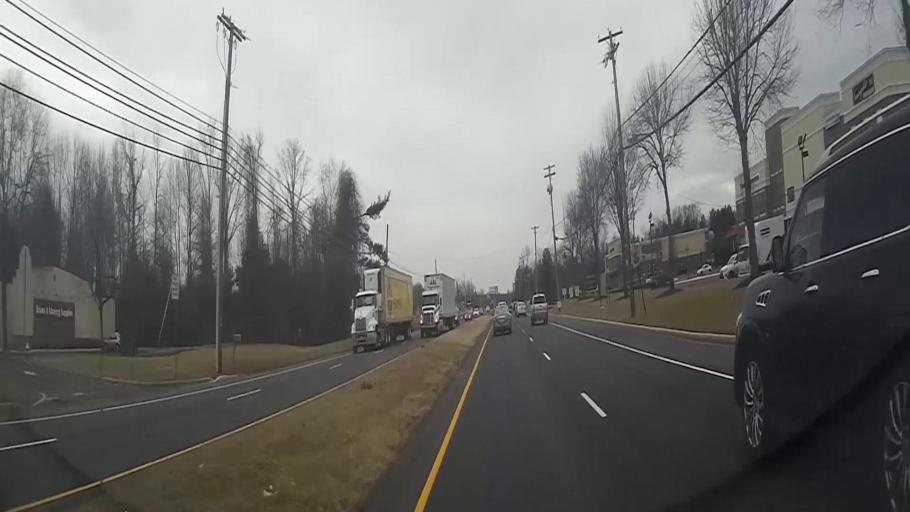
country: US
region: New Jersey
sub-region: Burlington County
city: Marlton
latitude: 39.8620
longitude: -74.9218
